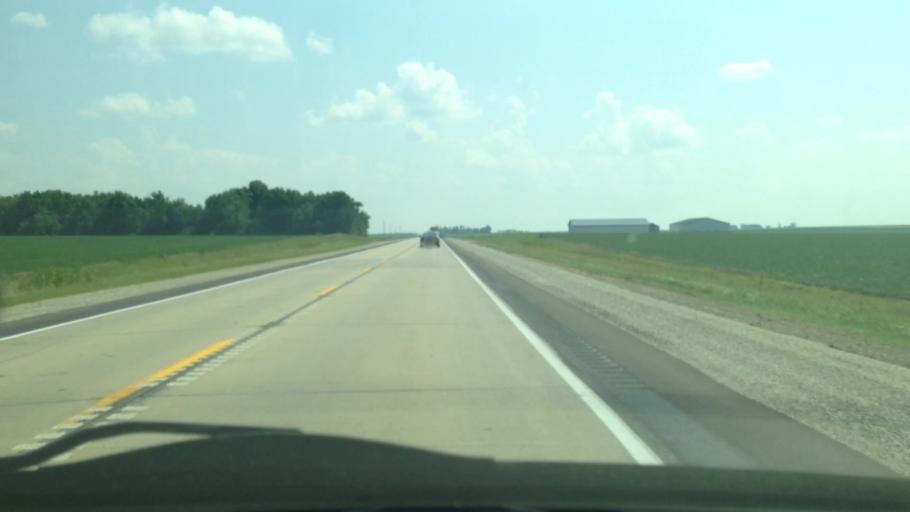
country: US
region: Iowa
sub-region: Howard County
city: Cresco
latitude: 43.4250
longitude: -92.2986
